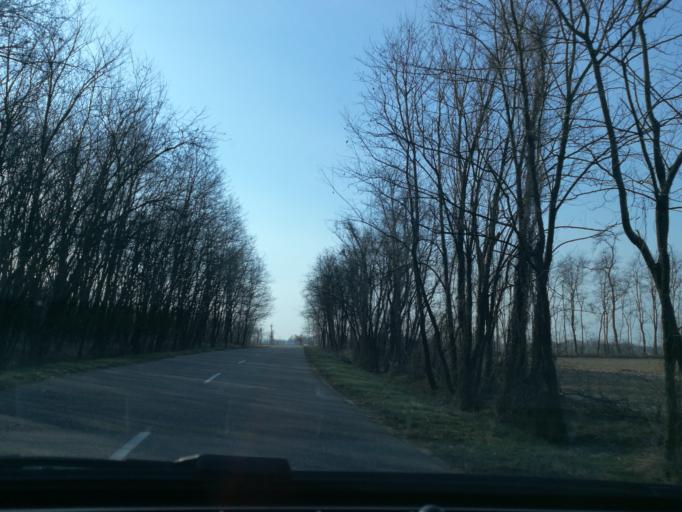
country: HU
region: Szabolcs-Szatmar-Bereg
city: Levelek
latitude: 47.9904
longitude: 21.9683
